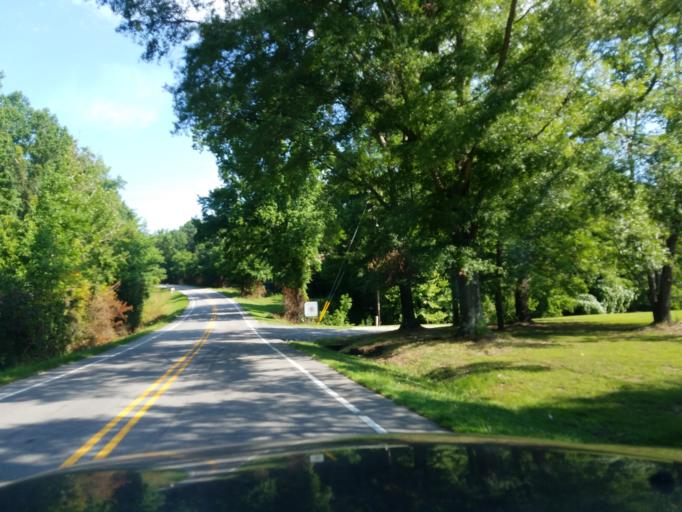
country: US
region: North Carolina
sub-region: Vance County
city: Henderson
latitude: 36.3472
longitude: -78.4146
